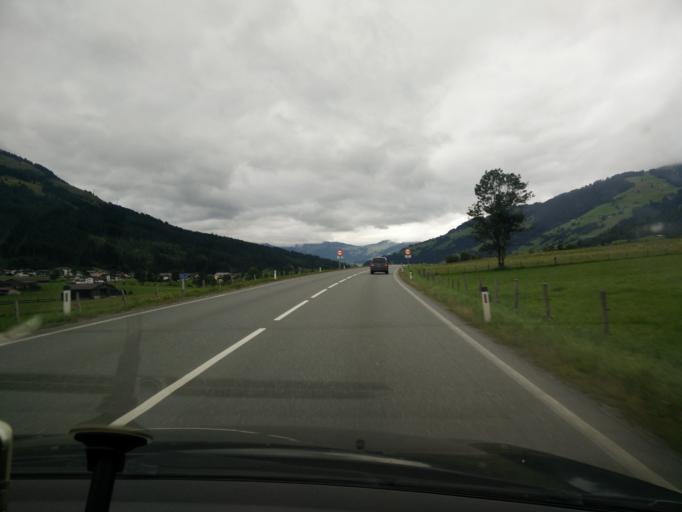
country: AT
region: Tyrol
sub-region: Politischer Bezirk Kitzbuhel
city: Brixen im Thale
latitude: 47.4507
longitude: 12.2779
